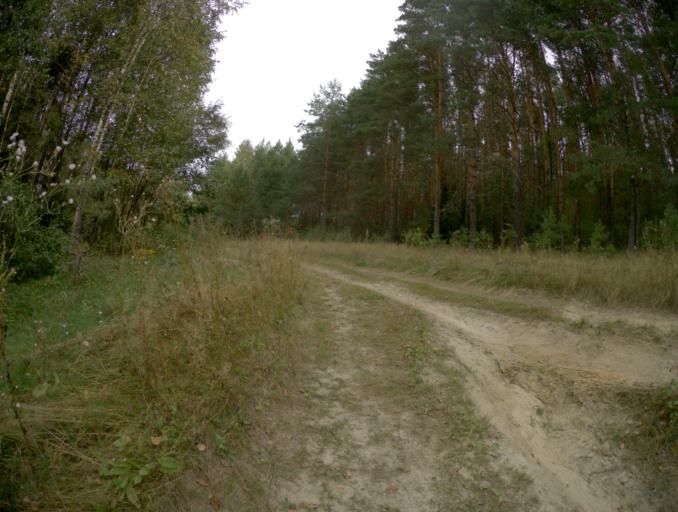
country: RU
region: Vladimir
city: Golovino
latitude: 55.9165
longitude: 40.4215
